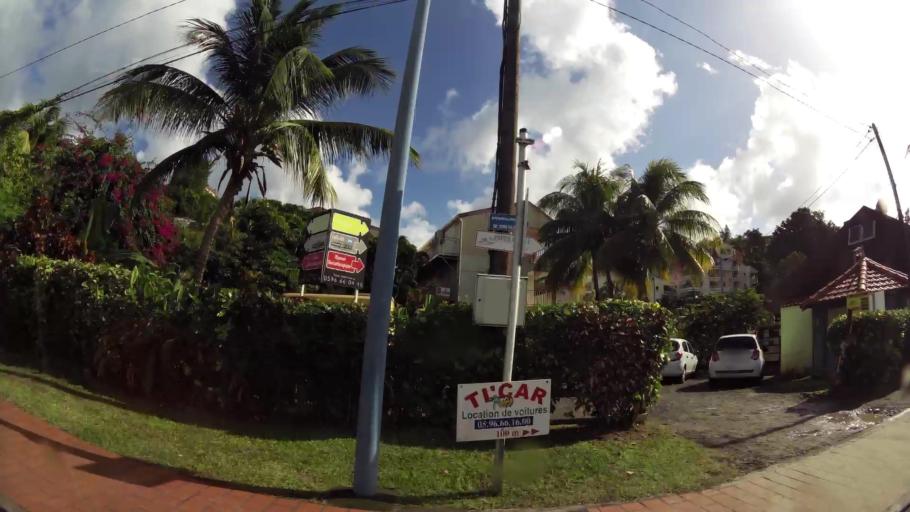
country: MQ
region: Martinique
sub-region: Martinique
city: Les Trois-Ilets
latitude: 14.5502
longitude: -61.0526
